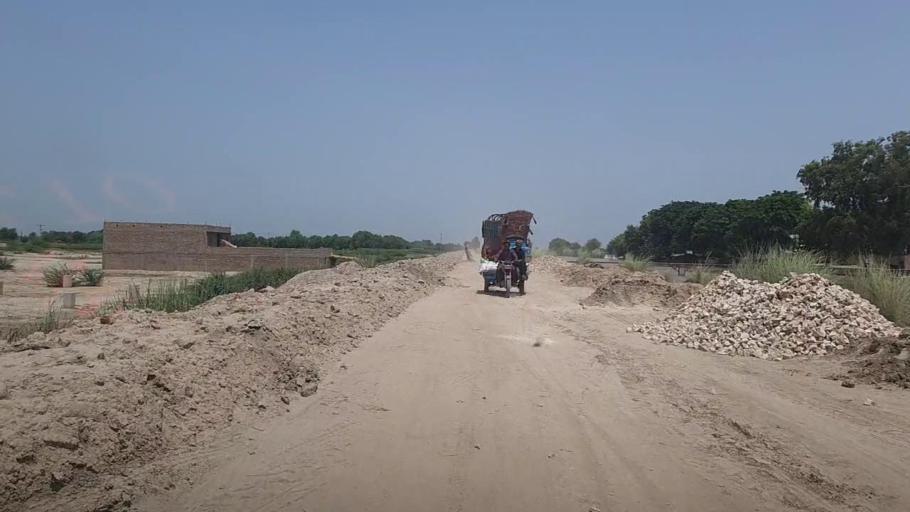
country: PK
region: Sindh
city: Pad Idan
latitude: 26.7843
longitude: 68.2779
